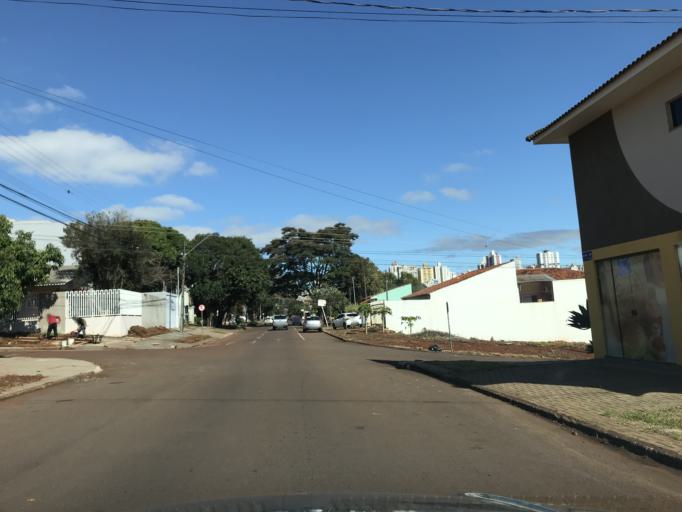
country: BR
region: Parana
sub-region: Cascavel
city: Cascavel
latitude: -24.9421
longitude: -53.4685
